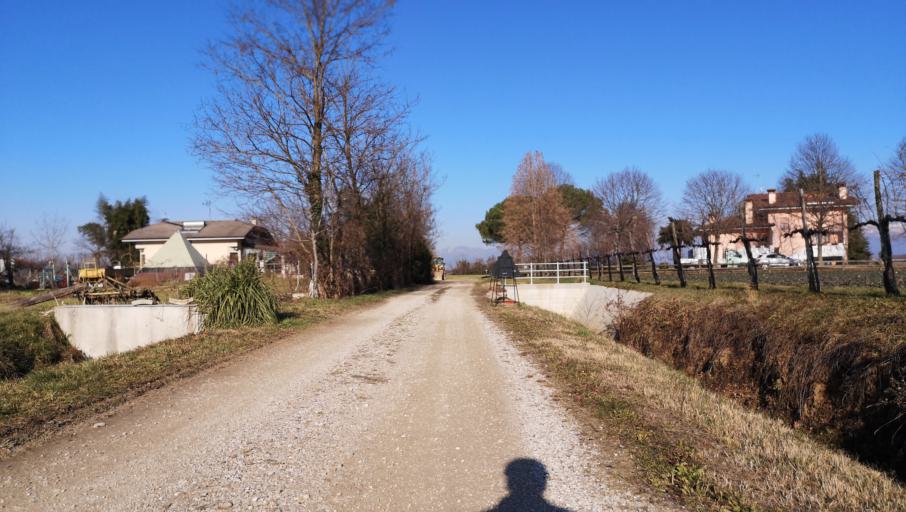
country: IT
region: Friuli Venezia Giulia
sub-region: Provincia di Udine
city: Lauzacco
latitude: 45.9766
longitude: 13.2905
